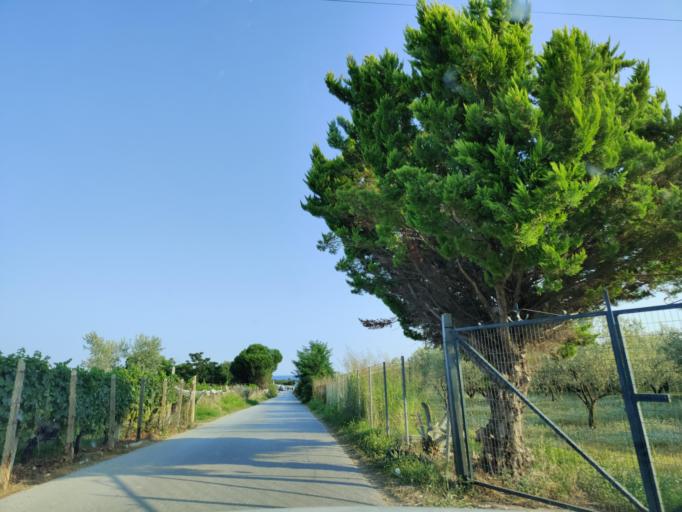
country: GR
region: East Macedonia and Thrace
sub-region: Nomos Kavalas
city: Nea Peramos
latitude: 40.8159
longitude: 24.2872
